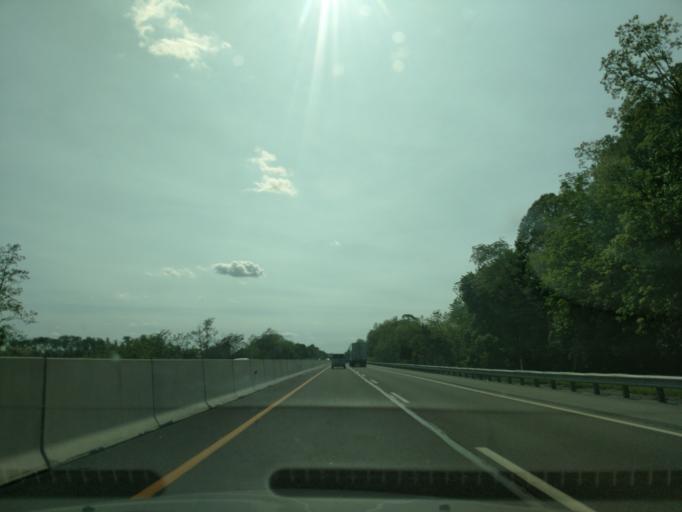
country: US
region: Pennsylvania
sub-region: Lancaster County
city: Clay
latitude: 40.2385
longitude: -76.2638
